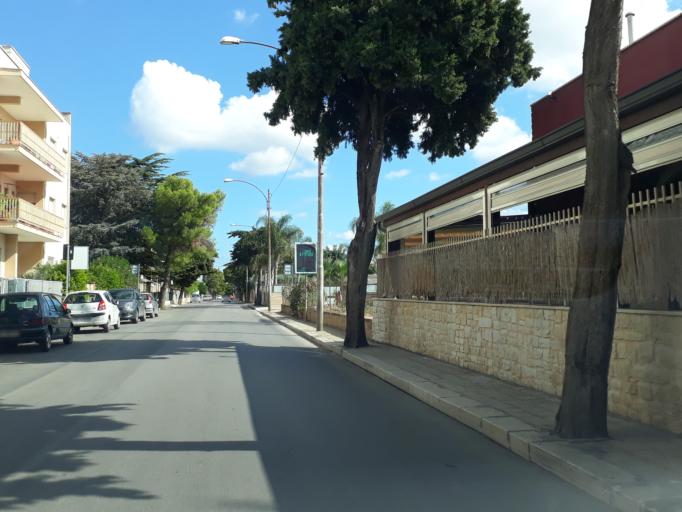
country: IT
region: Apulia
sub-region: Provincia di Bari
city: Rutigliano
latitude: 41.0127
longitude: 17.0122
